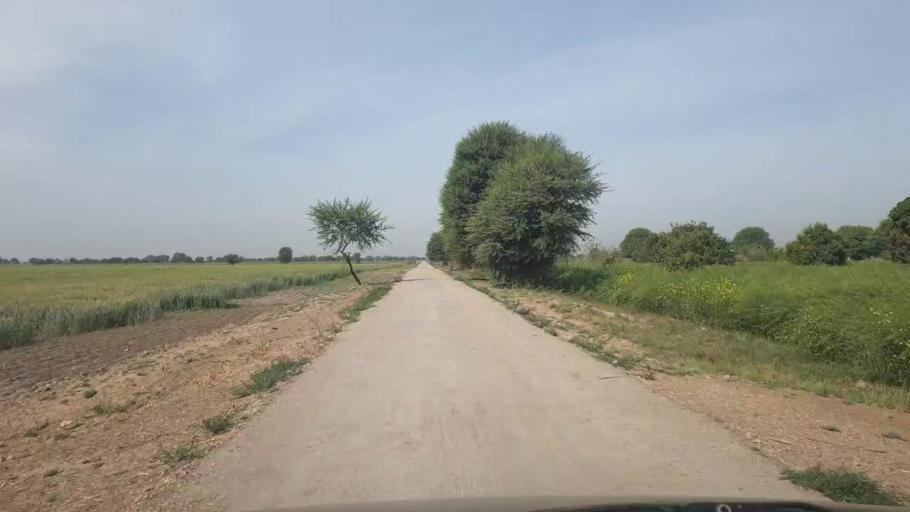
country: PK
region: Sindh
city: Umarkot
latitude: 25.2873
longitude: 69.6966
